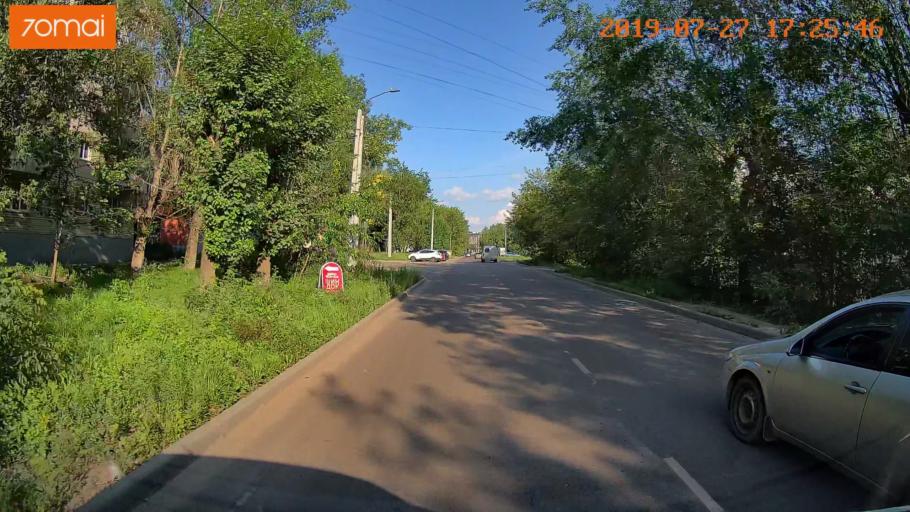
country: RU
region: Ivanovo
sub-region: Gorod Ivanovo
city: Ivanovo
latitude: 57.0162
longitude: 40.9635
